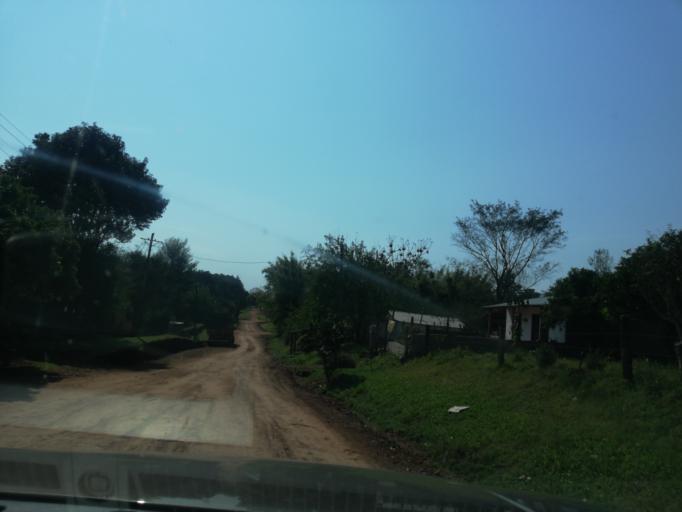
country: AR
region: Misiones
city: Bonpland
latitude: -27.4816
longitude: -55.4791
